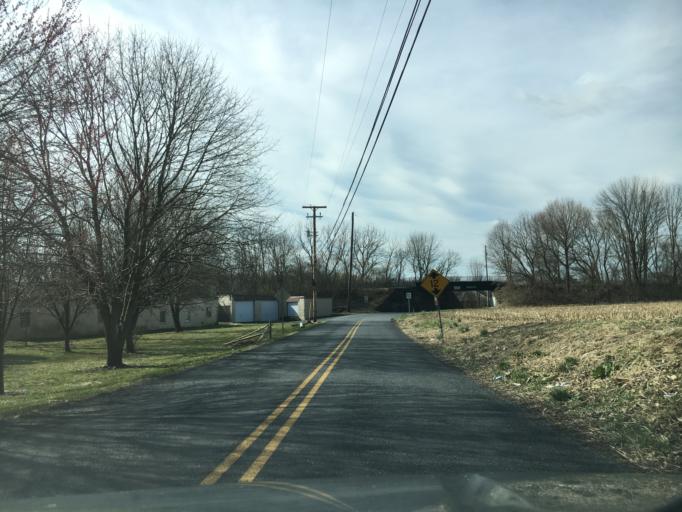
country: US
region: Pennsylvania
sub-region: Northampton County
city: North Catasauqua
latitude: 40.6871
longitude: -75.4529
